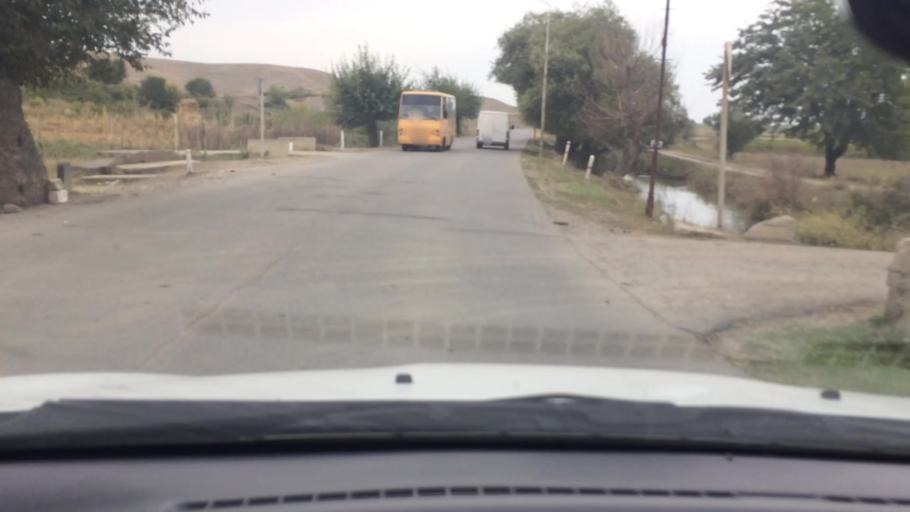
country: AM
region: Tavush
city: Berdavan
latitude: 41.3344
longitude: 45.0345
